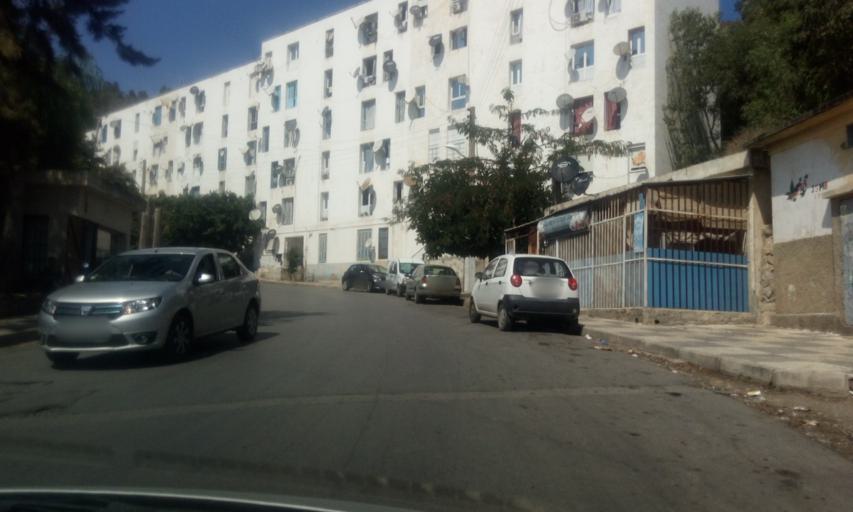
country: DZ
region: Bejaia
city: Bejaia
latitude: 36.7597
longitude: 5.0869
